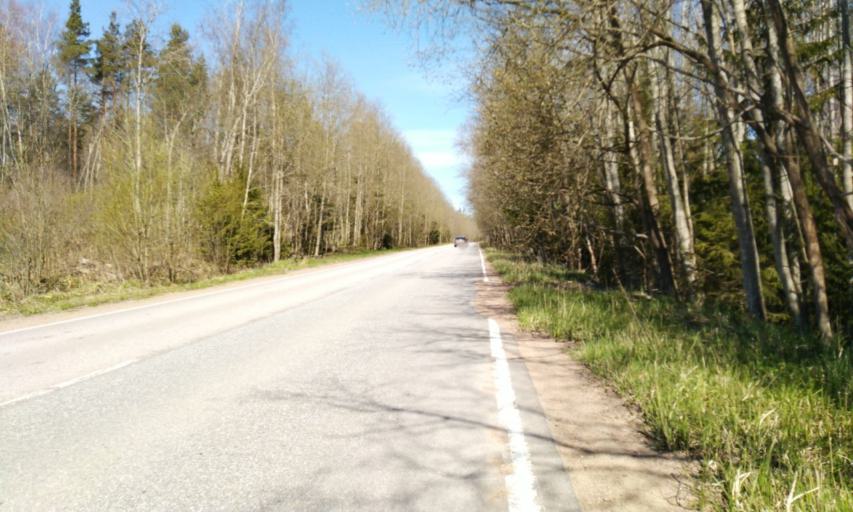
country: RU
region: Leningrad
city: Garbolovo
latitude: 60.4063
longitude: 30.4665
